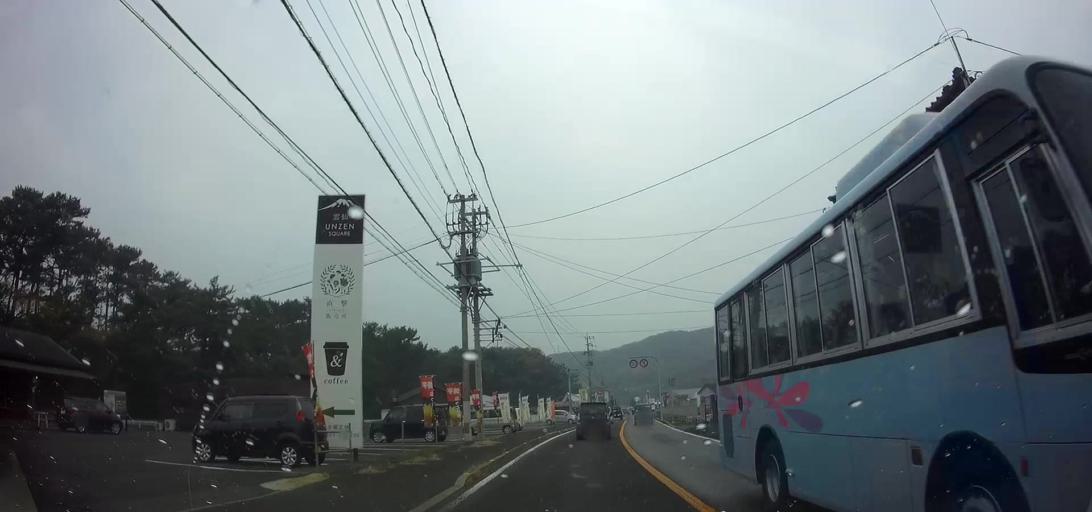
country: JP
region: Nagasaki
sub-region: Isahaya-shi
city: Isahaya
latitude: 32.7898
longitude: 130.1878
